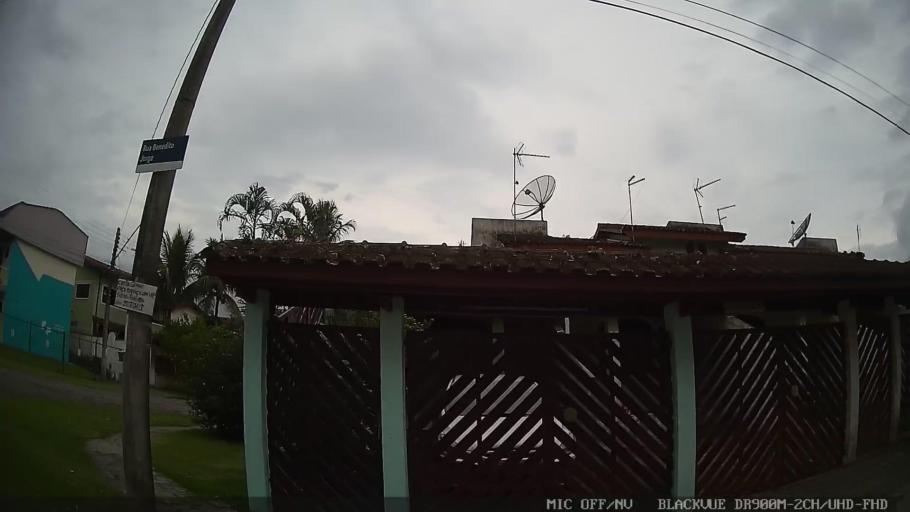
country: BR
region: Sao Paulo
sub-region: Caraguatatuba
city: Caraguatatuba
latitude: -23.6287
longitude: -45.3902
